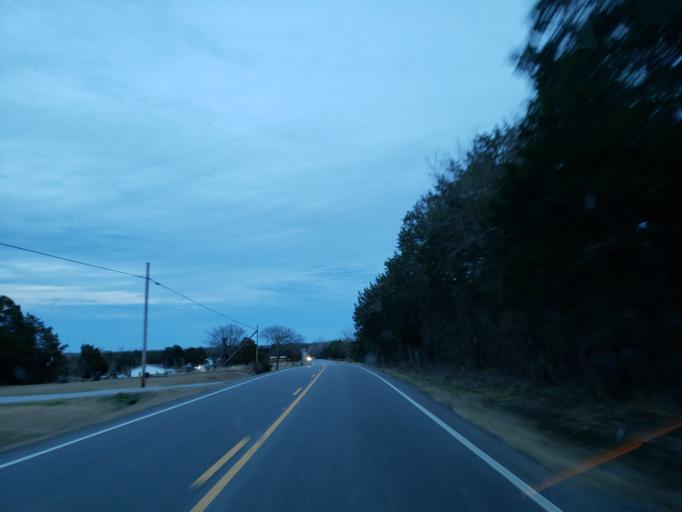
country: US
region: Alabama
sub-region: Sumter County
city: Livingston
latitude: 32.8099
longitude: -88.2305
